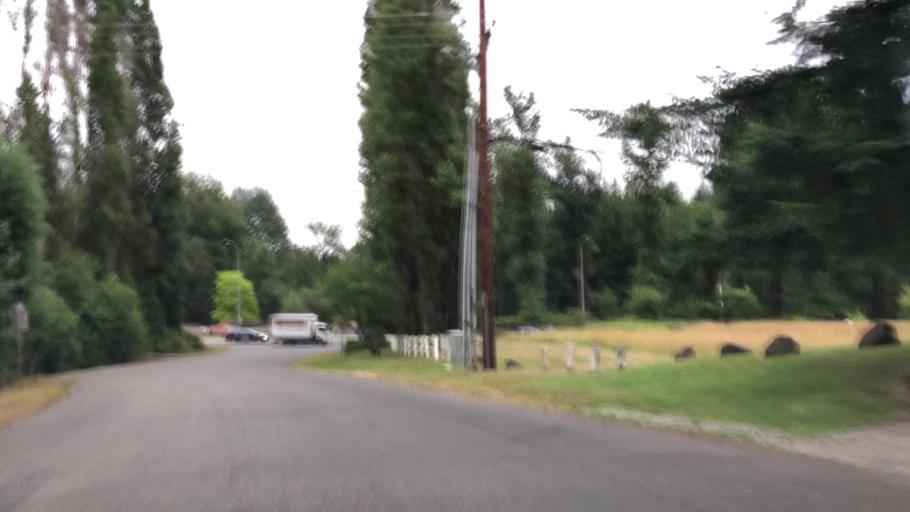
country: US
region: Washington
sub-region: King County
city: Cottage Lake
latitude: 47.7185
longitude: -122.0890
